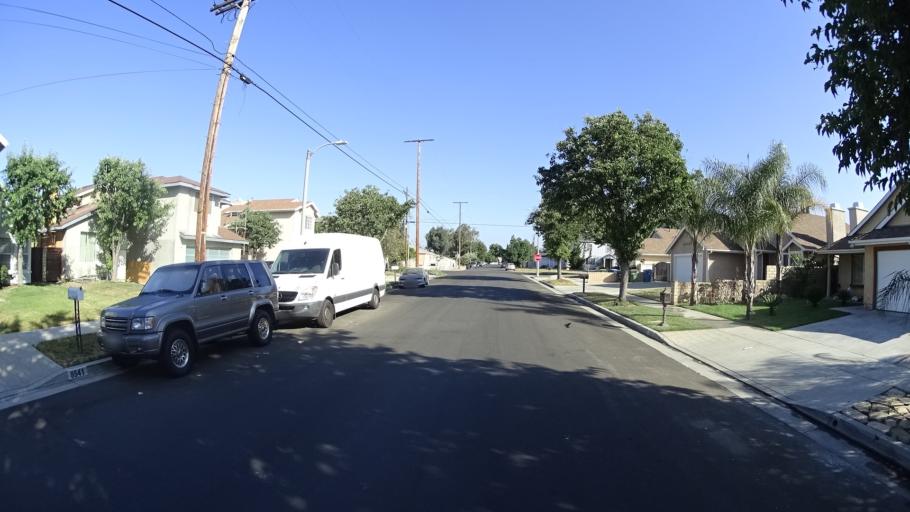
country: US
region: California
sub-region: Los Angeles County
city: Van Nuys
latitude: 34.2252
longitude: -118.4228
